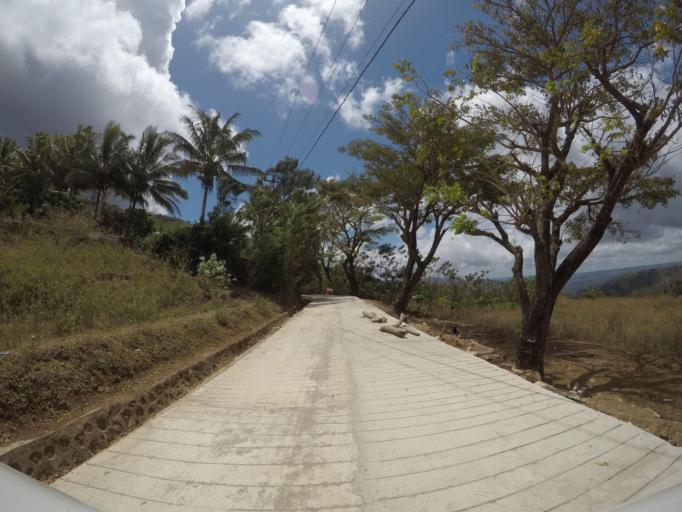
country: TL
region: Lautem
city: Lospalos
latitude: -8.5537
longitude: 126.8290
